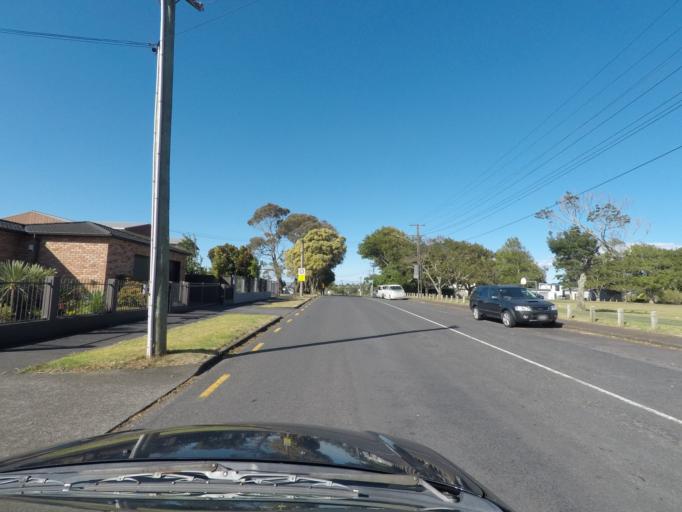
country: NZ
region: Auckland
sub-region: Auckland
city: Rosebank
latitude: -36.8865
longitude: 174.6864
